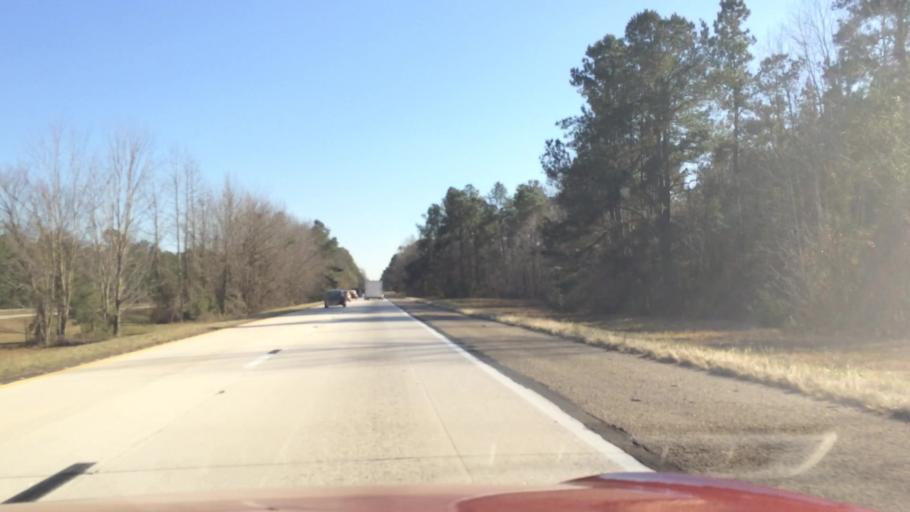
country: US
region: South Carolina
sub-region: Orangeburg County
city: Holly Hill
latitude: 33.2597
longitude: -80.4766
